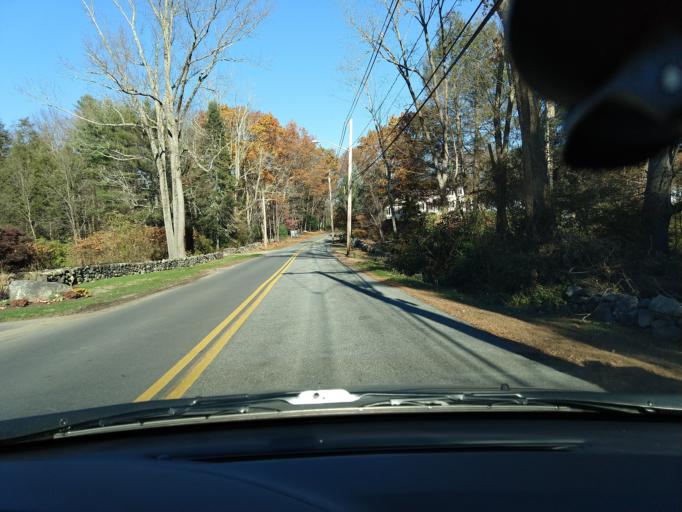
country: US
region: Massachusetts
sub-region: Middlesex County
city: Concord
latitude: 42.4879
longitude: -71.3349
